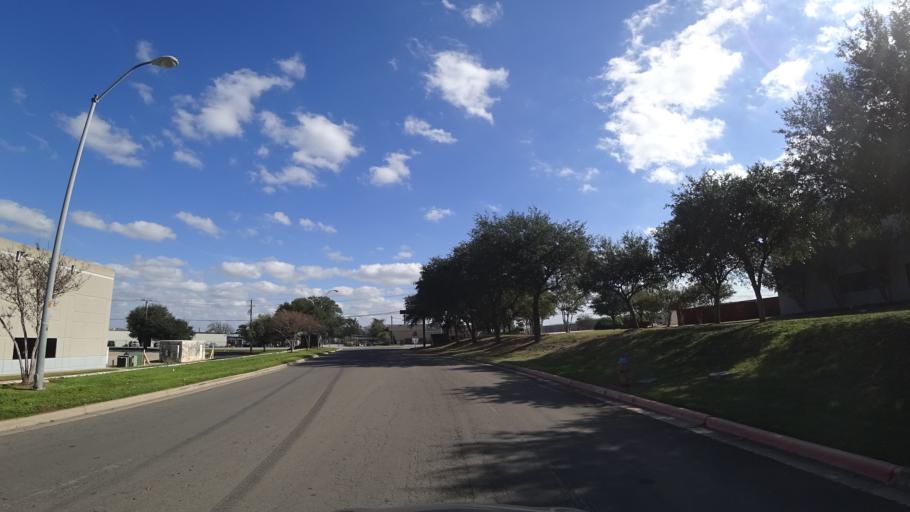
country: US
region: Texas
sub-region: Travis County
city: Wells Branch
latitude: 30.4713
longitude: -97.6749
